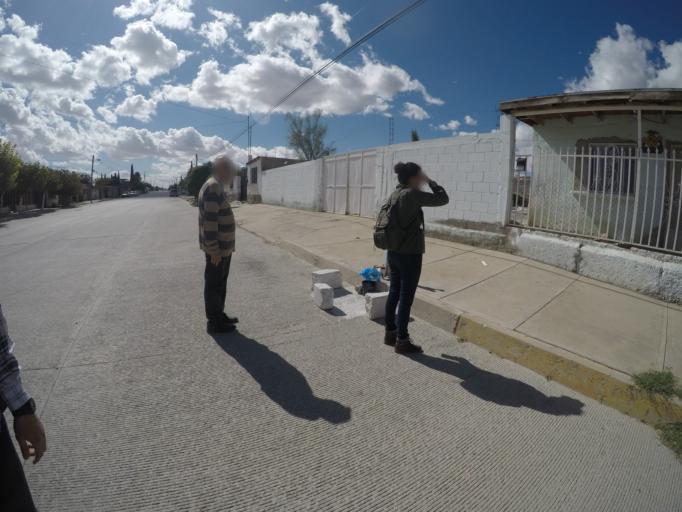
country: MX
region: Chihuahua
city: Ciudad Juarez
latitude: 31.6894
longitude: -106.4840
